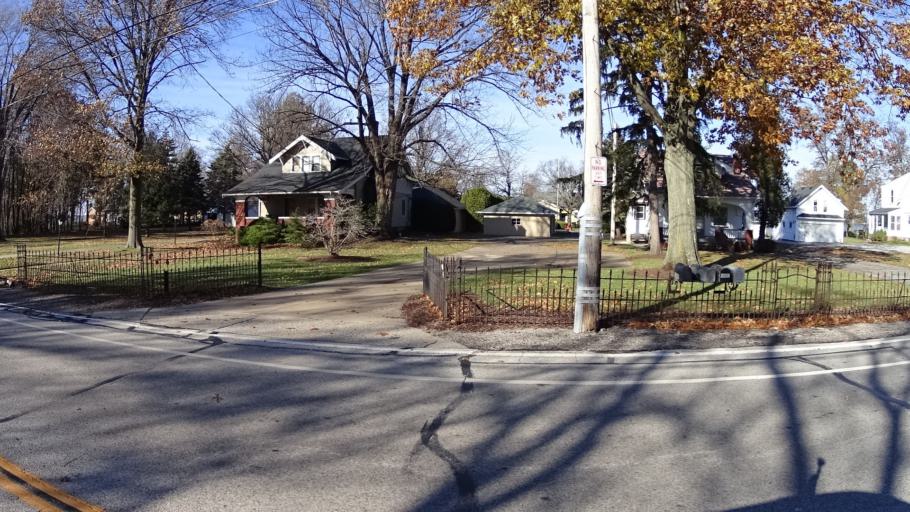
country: US
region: Ohio
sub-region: Lorain County
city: Avon Lake
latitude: 41.5138
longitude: -82.0051
